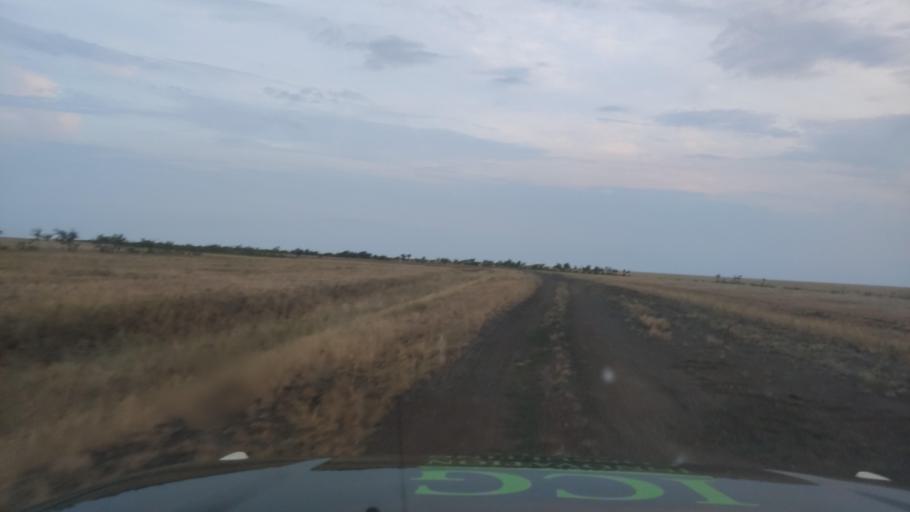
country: KZ
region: Pavlodar
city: Pavlodar
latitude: 52.1799
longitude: 77.6003
